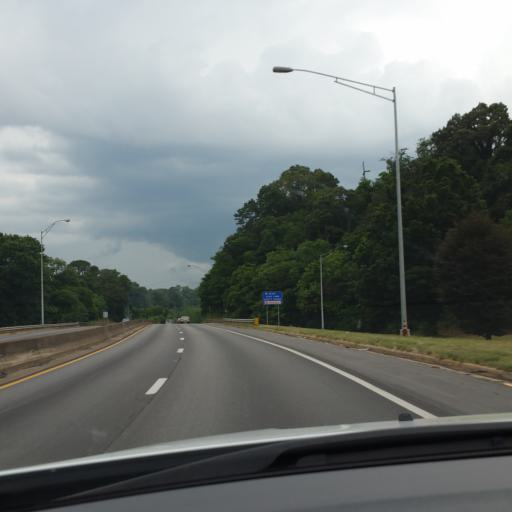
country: US
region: North Carolina
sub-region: Buncombe County
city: Asheville
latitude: 35.5958
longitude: -82.5698
